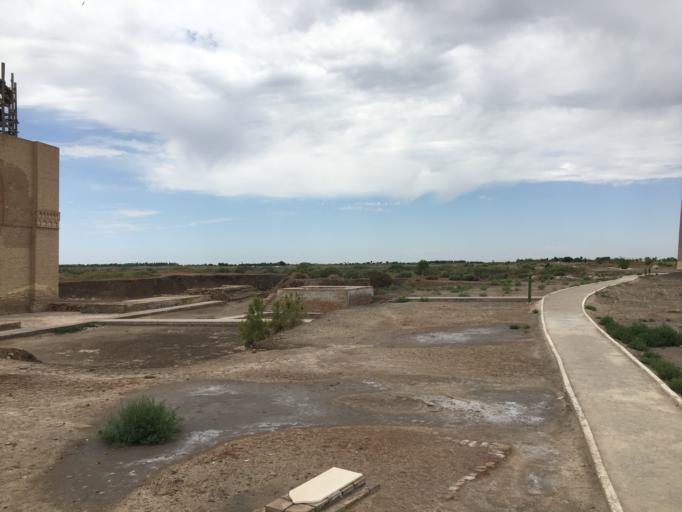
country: TM
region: Dasoguz
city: Koeneuergench
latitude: 42.3078
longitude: 59.1443
